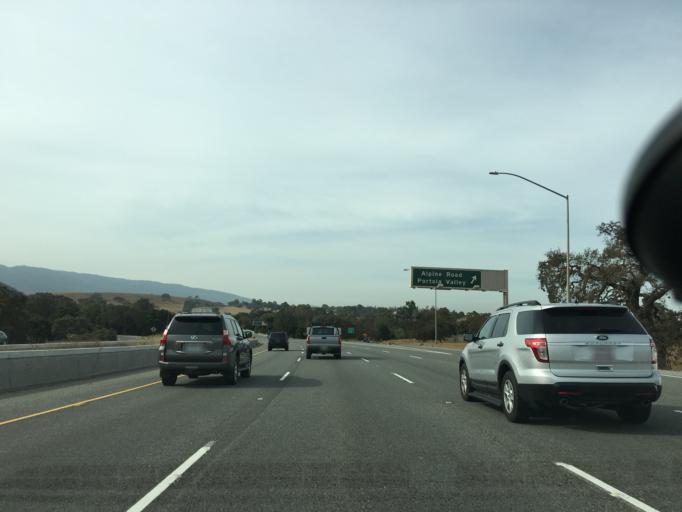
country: US
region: California
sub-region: San Mateo County
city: Ladera
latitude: 37.4077
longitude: -122.1905
